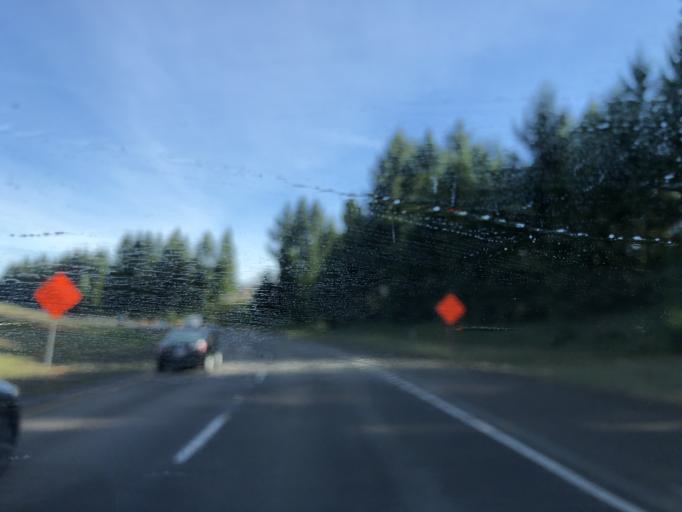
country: US
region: Oregon
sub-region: Washington County
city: Tualatin
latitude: 45.3680
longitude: -122.7561
